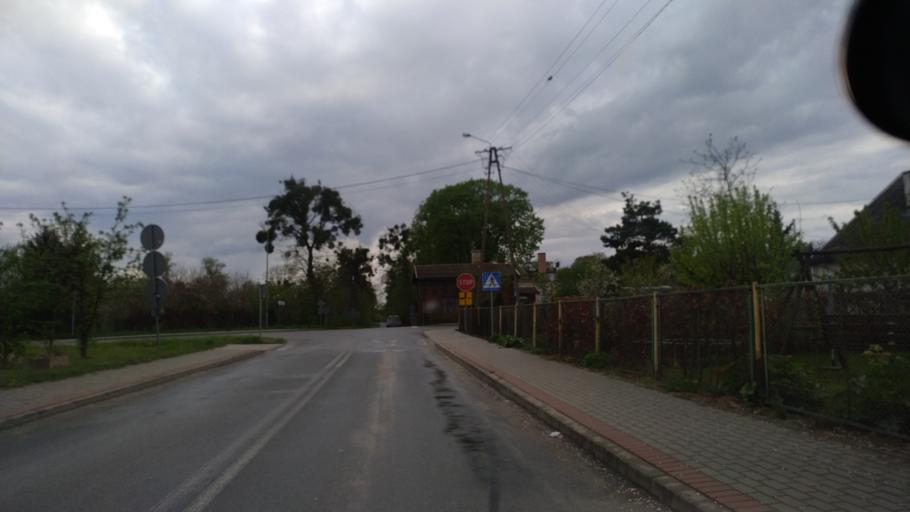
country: PL
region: Pomeranian Voivodeship
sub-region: Powiat starogardzki
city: Smetowo Graniczne
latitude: 53.7376
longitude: 18.6493
